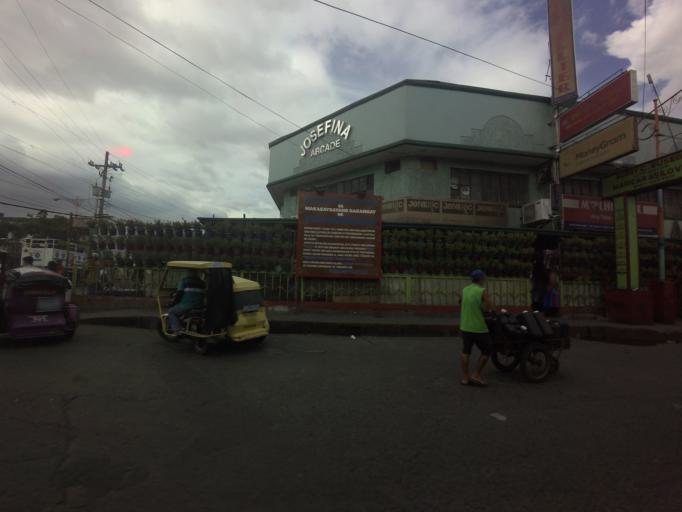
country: PH
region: Calabarzon
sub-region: Province of Rizal
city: Pateros
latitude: 14.5574
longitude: 121.0847
